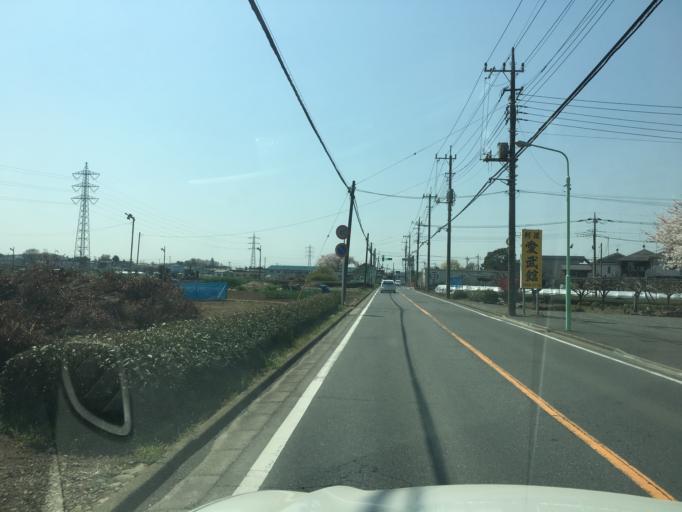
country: JP
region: Saitama
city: Sayama
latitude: 35.8342
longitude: 139.4352
